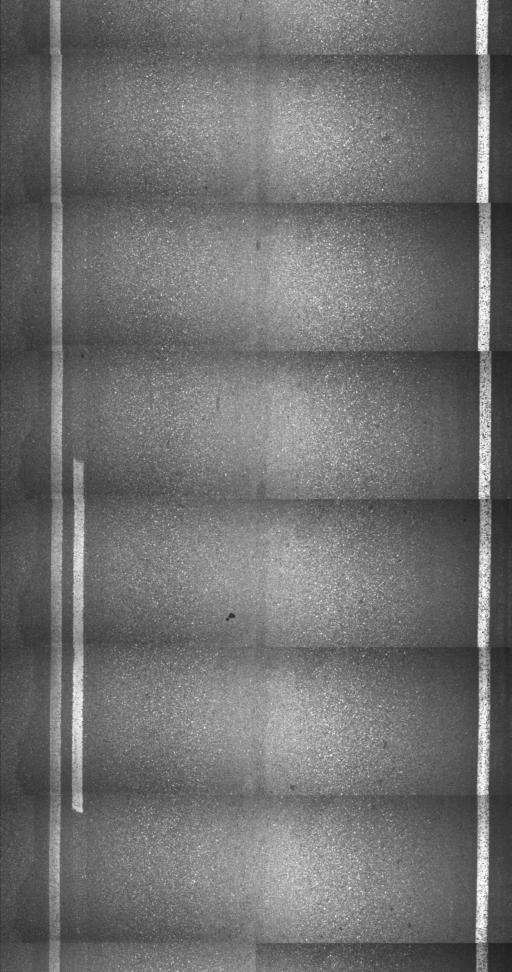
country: US
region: Vermont
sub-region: Lamoille County
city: Hyde Park
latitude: 44.7300
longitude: -72.4911
